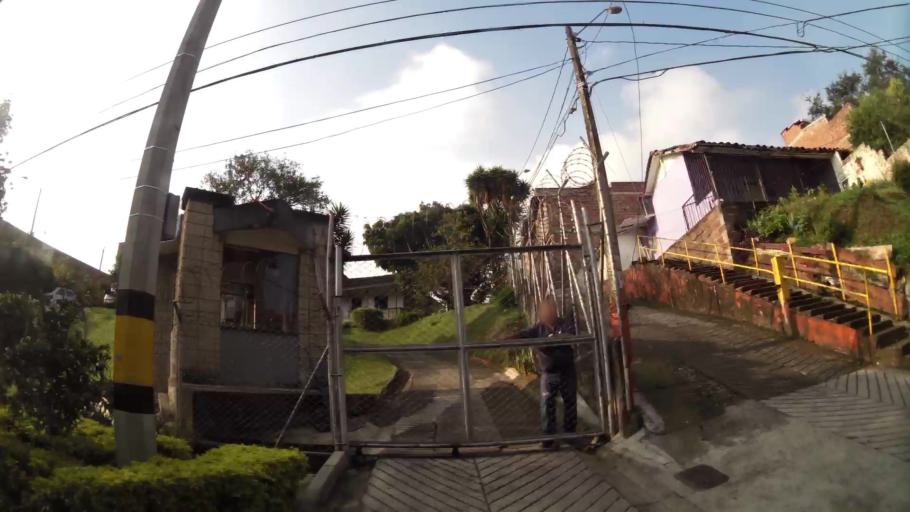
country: CO
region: Antioquia
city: Sabaneta
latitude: 6.1630
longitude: -75.6207
